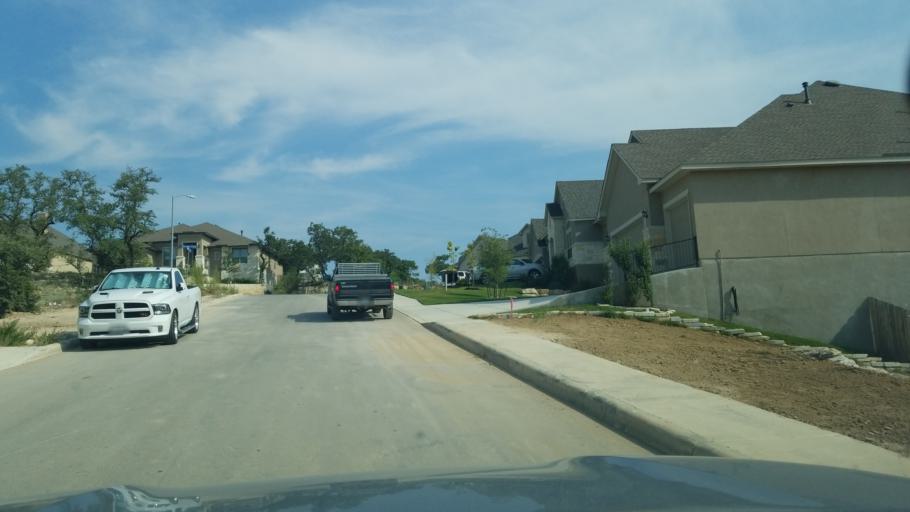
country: US
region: Texas
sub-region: Bexar County
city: Scenic Oaks
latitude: 29.7172
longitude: -98.6557
